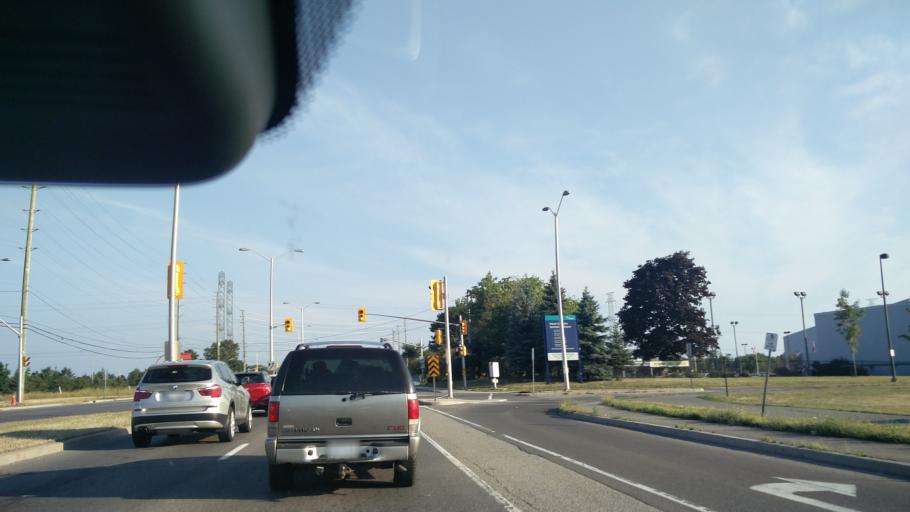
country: CA
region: Ontario
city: Bells Corners
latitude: 45.3252
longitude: -75.7466
